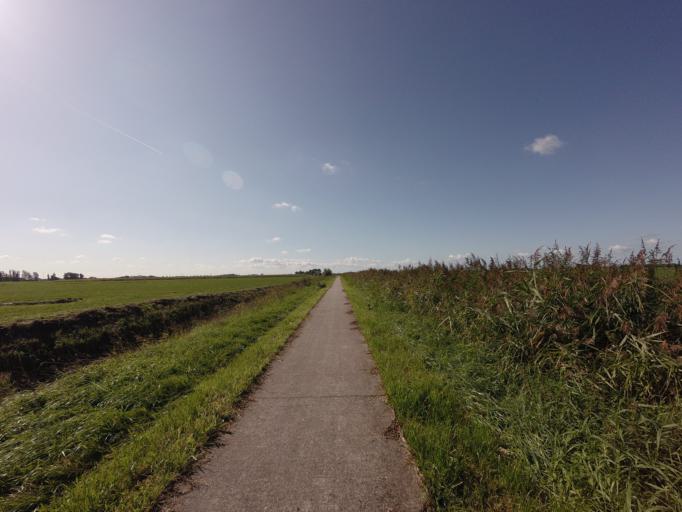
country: NL
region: Friesland
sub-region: Gemeente Boarnsterhim
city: Reduzum
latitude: 53.1355
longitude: 5.7590
